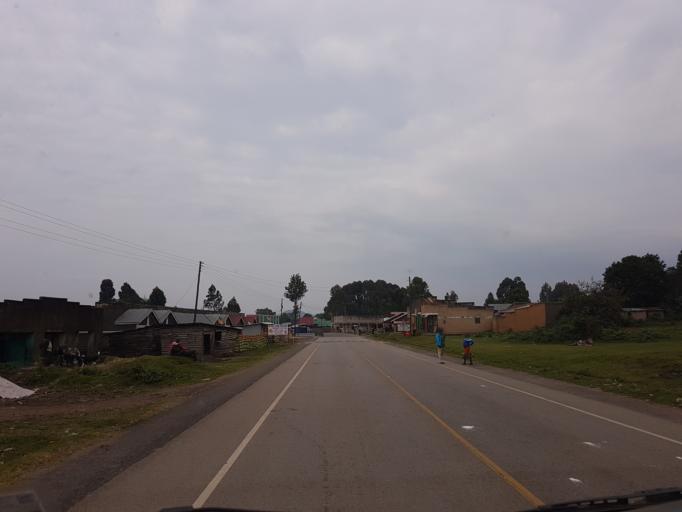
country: UG
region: Western Region
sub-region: Kisoro District
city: Kisoro
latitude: -1.3377
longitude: 29.7383
